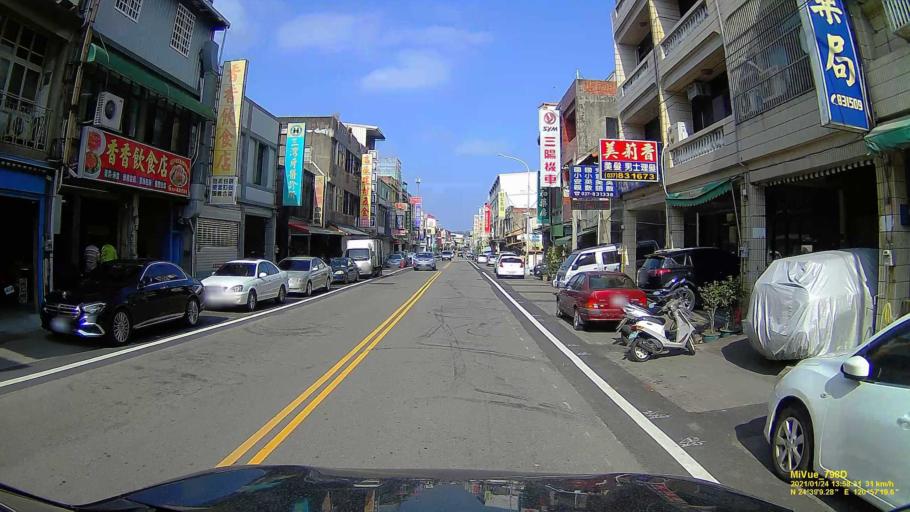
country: TW
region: Taiwan
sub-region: Hsinchu
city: Hsinchu
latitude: 24.6528
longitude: 120.9555
